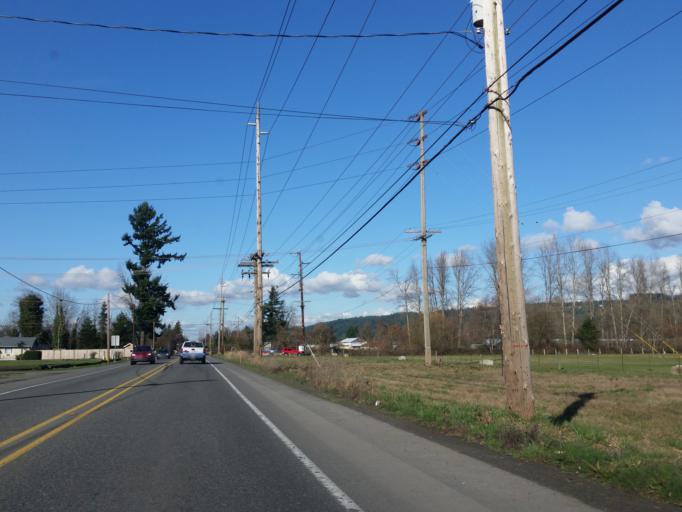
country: US
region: Washington
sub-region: Pierce County
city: Alderton
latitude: 47.1831
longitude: -122.2293
